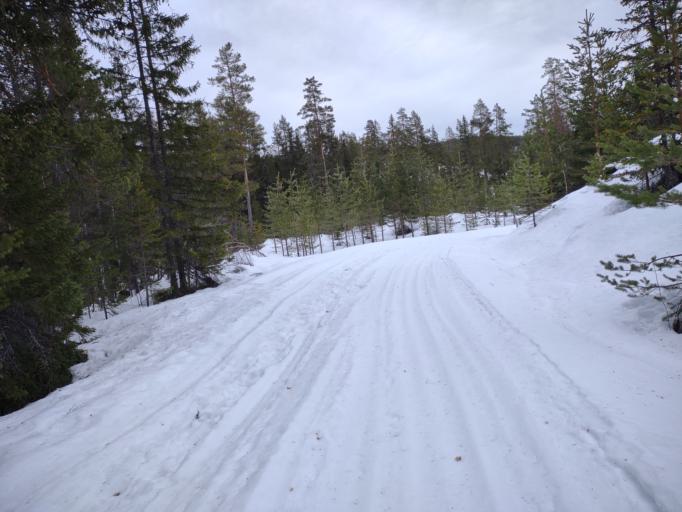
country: NO
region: Buskerud
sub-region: Flesberg
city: Lampeland
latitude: 59.7271
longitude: 9.5351
